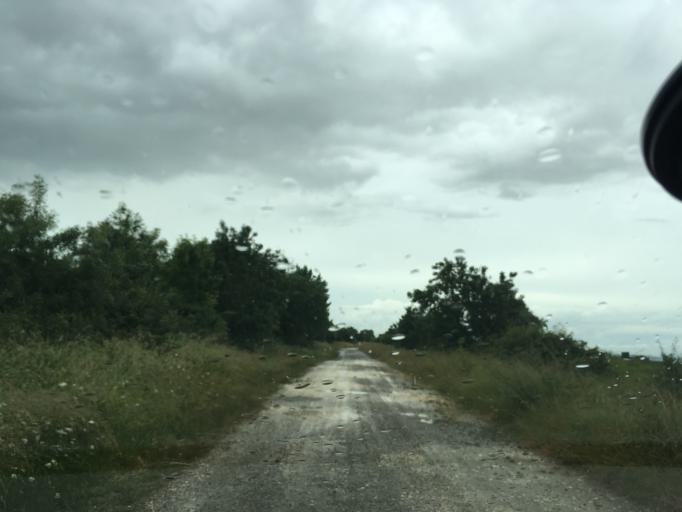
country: FR
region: Aquitaine
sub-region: Departement de la Gironde
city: Saint-Estephe
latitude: 45.3352
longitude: -0.7980
